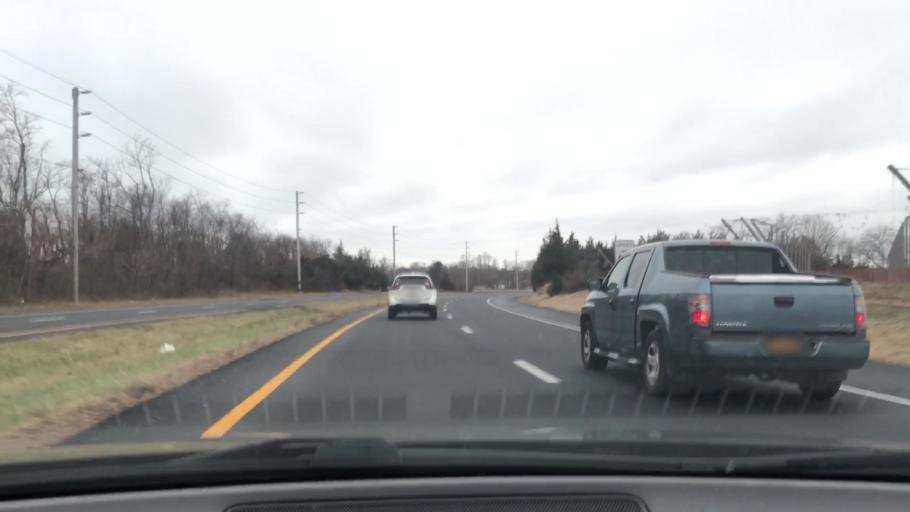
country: US
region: New York
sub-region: Suffolk County
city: Mattituck
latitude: 41.0040
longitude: -72.5241
